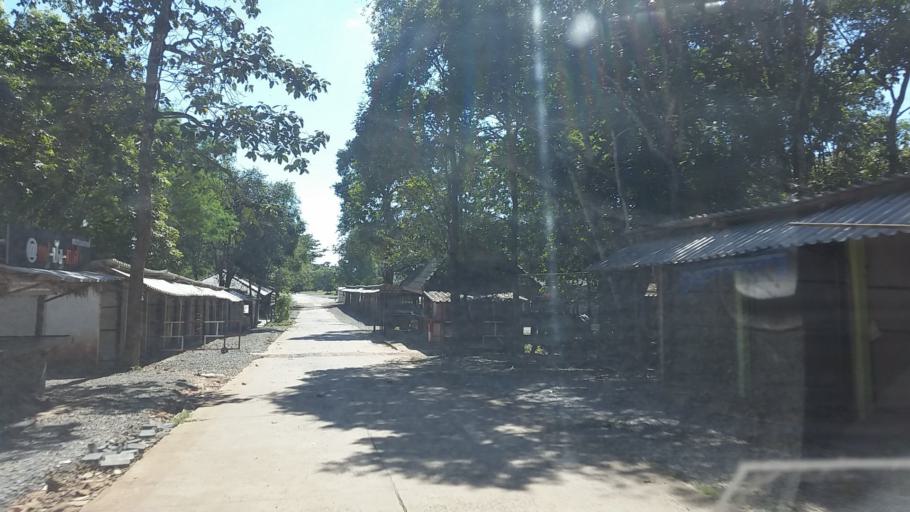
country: TH
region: Chaiyaphum
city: Sap Yai
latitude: 15.6332
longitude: 101.3948
